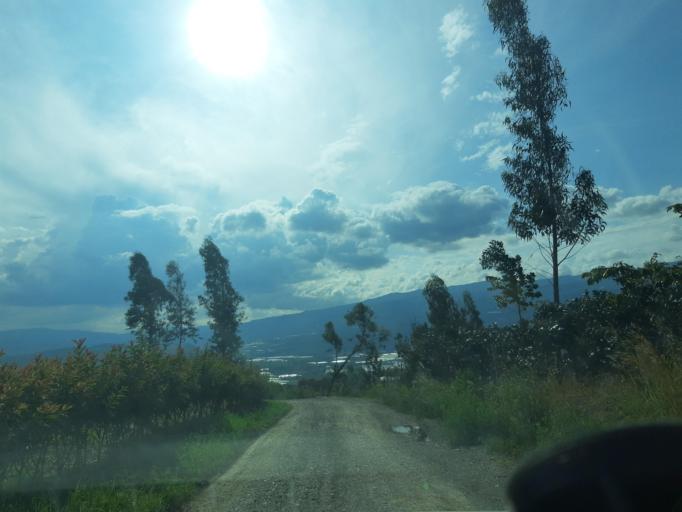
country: CO
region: Boyaca
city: Villa de Leiva
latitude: 5.6661
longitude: -73.5582
